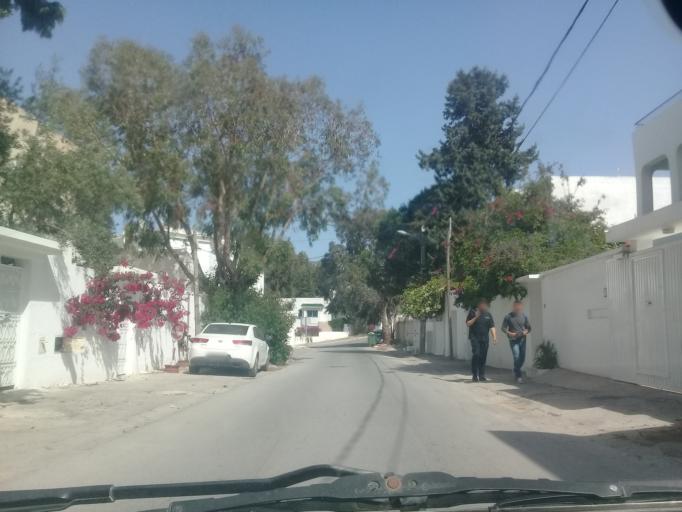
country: TN
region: Tunis
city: Sidi Bou Said
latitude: 36.8810
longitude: 10.3381
